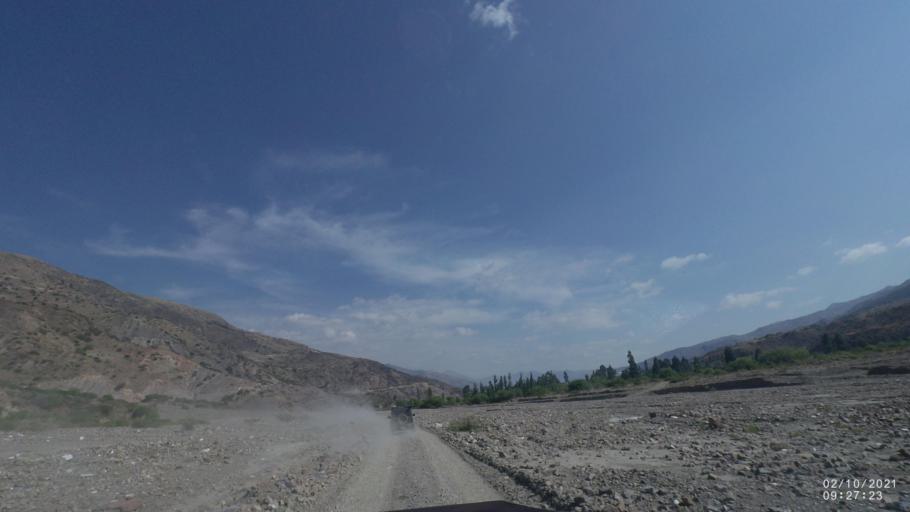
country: BO
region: Cochabamba
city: Irpa Irpa
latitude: -17.8559
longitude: -66.3151
